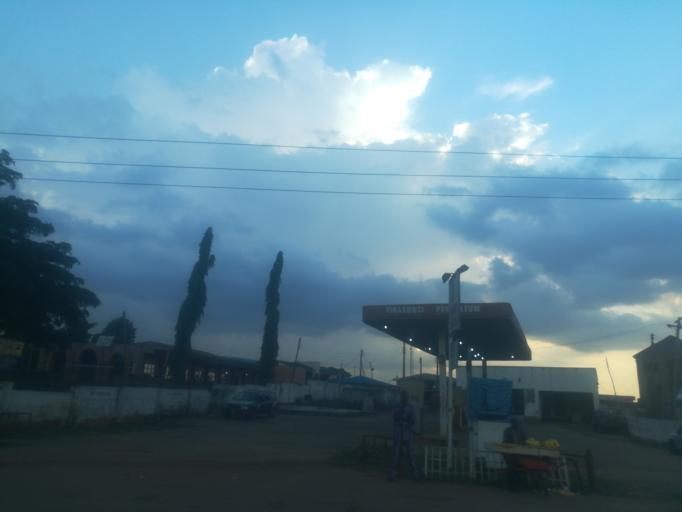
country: NG
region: Oyo
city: Ibadan
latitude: 7.4449
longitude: 3.9212
